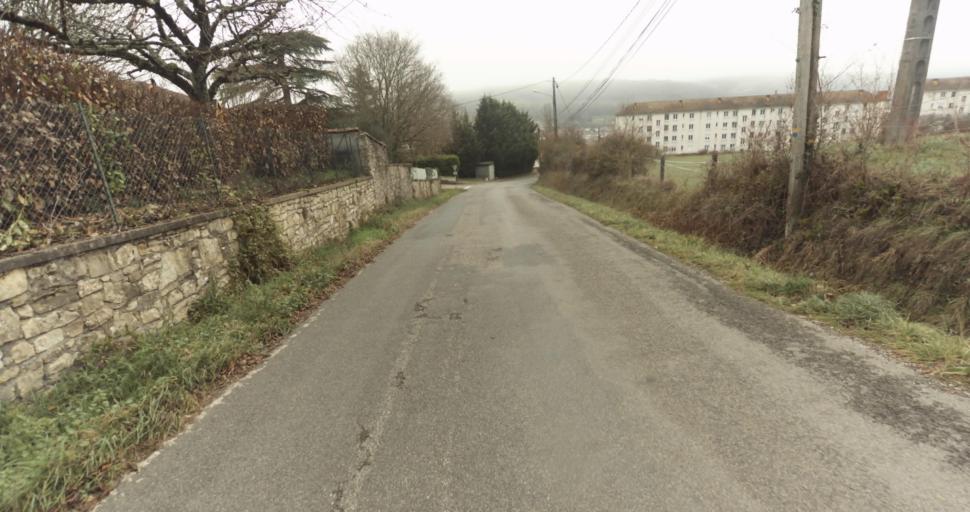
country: FR
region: Midi-Pyrenees
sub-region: Departement du Lot
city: Figeac
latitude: 44.6171
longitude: 2.0255
